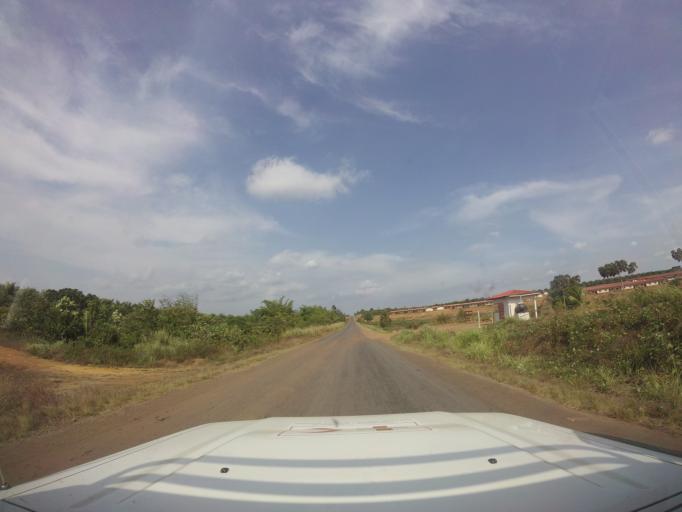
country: LR
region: Bomi
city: Tubmanburg
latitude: 6.7301
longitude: -11.0137
